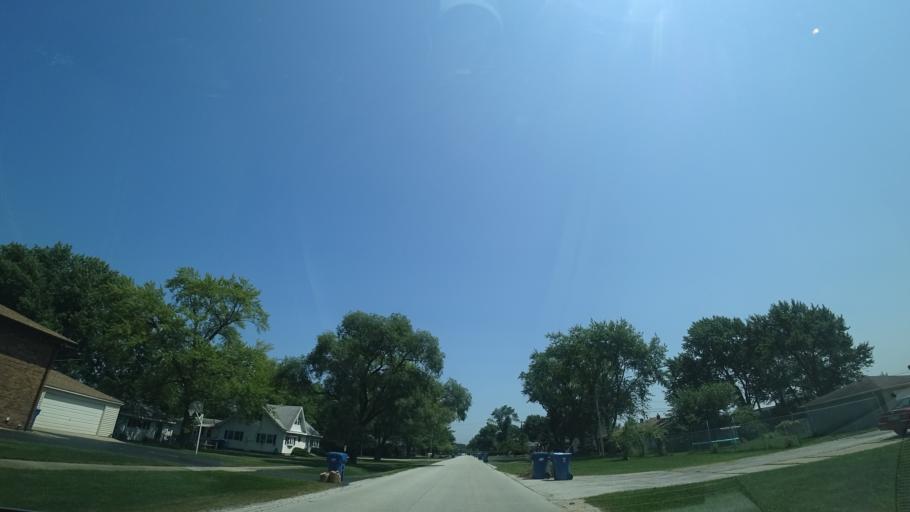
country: US
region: Illinois
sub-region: Cook County
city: Alsip
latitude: 41.6763
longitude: -87.7438
